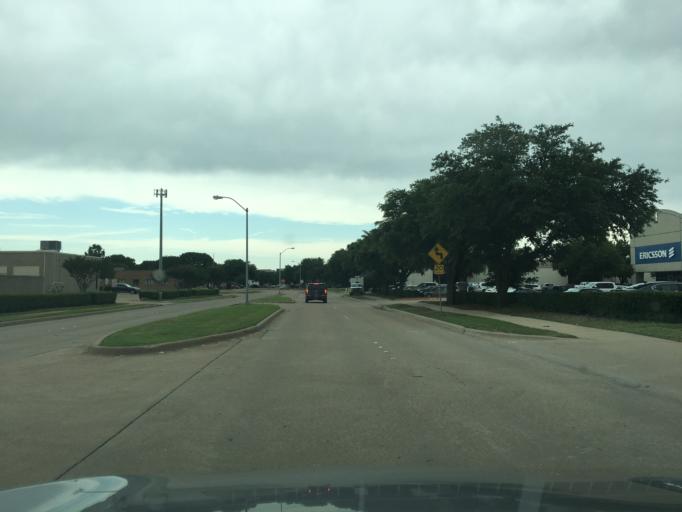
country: US
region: Texas
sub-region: Dallas County
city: Richardson
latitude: 32.9649
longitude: -96.7052
